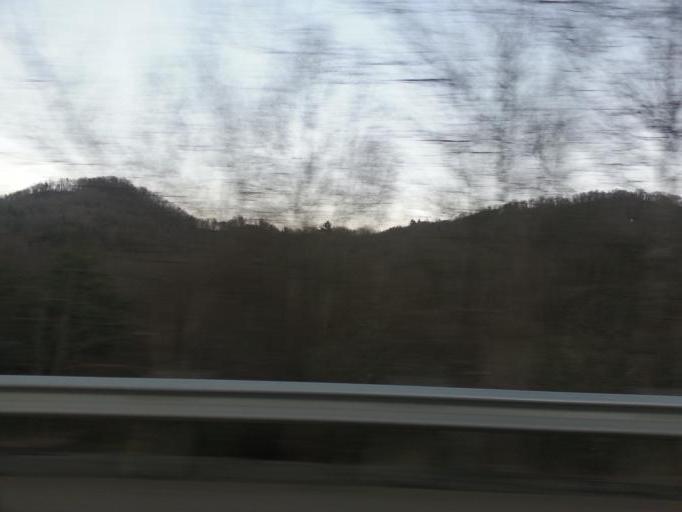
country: US
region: North Carolina
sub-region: Haywood County
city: Cove Creek
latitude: 35.5919
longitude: -82.9989
